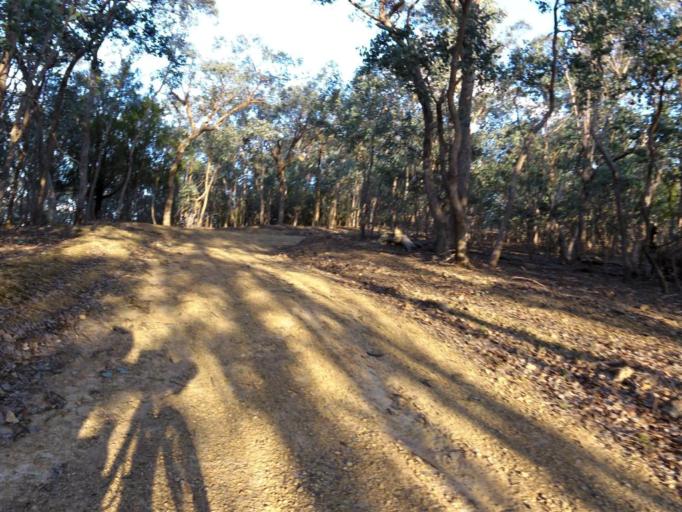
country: AU
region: Victoria
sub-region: Nillumbik
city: North Warrandyte
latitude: -37.7242
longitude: 145.2387
